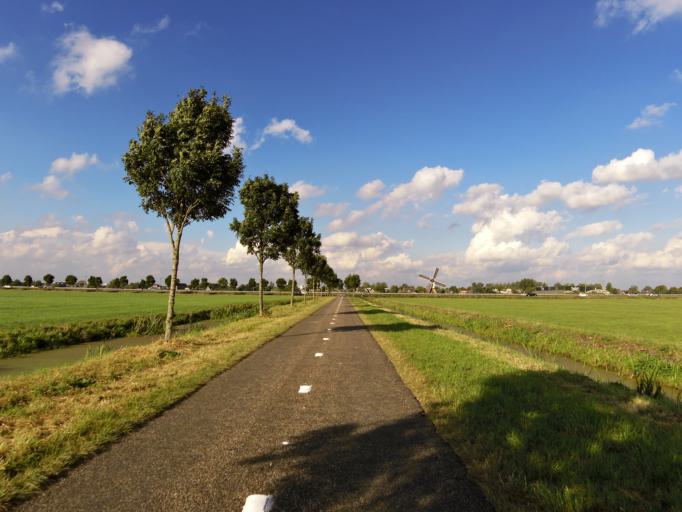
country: NL
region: South Holland
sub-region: Gemeente Rijnwoude
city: Benthuizen
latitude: 52.1224
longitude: 4.5629
